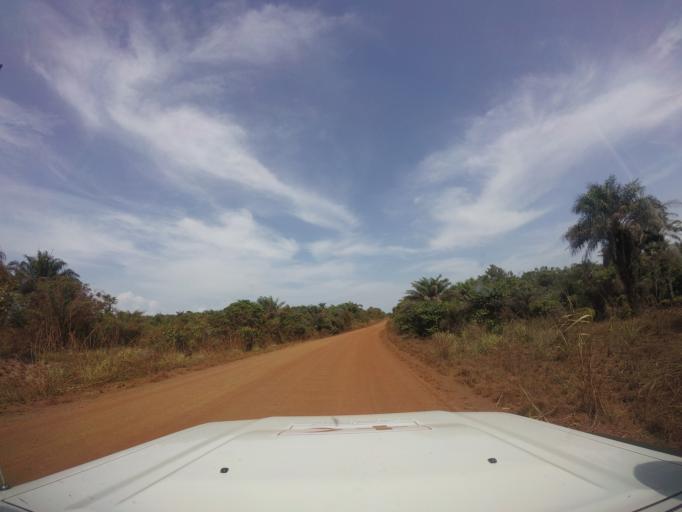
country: LR
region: Grand Cape Mount
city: Robertsport
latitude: 6.6912
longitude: -11.2638
